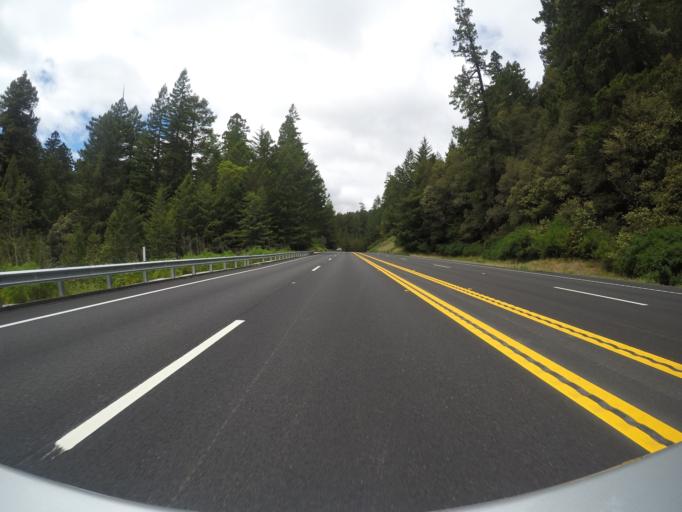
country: US
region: California
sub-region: Humboldt County
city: Rio Dell
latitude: 40.3358
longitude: -123.9316
